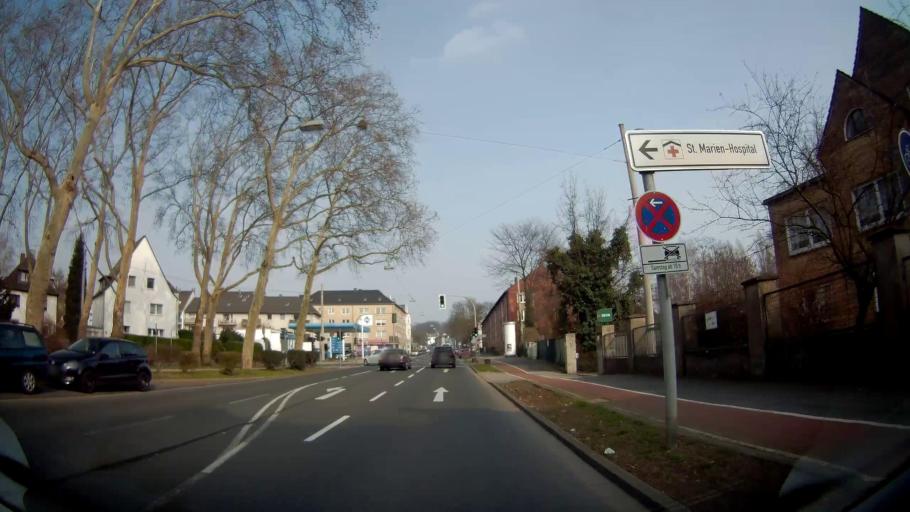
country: DE
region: North Rhine-Westphalia
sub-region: Regierungsbezirk Dusseldorf
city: Oberhausen
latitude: 51.5024
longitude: 6.8919
